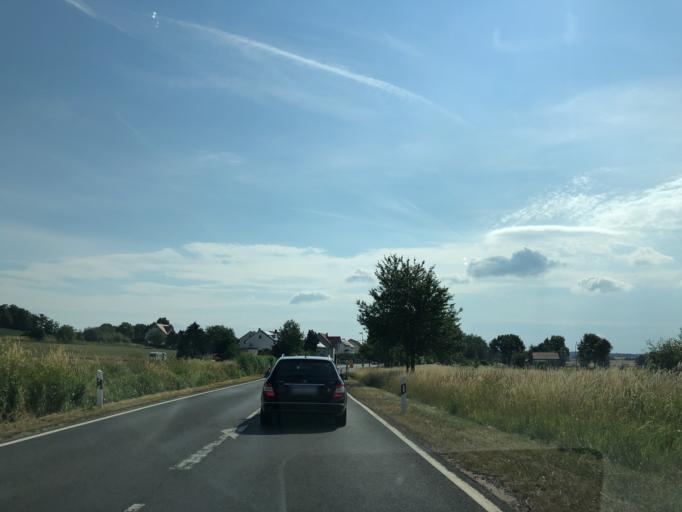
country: DE
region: Bavaria
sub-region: Upper Franconia
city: Schlusselfeld
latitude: 49.7451
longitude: 10.6641
